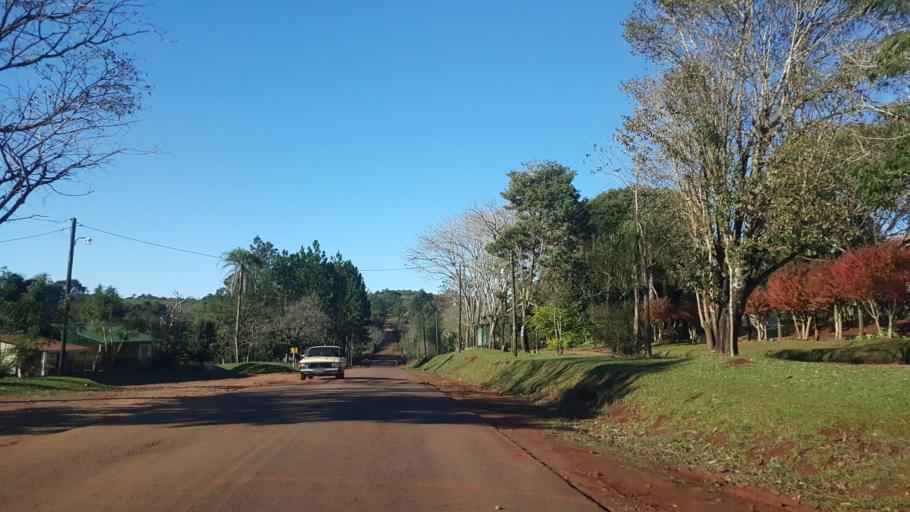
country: AR
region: Misiones
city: Jardin America
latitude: -27.0916
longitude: -55.2855
